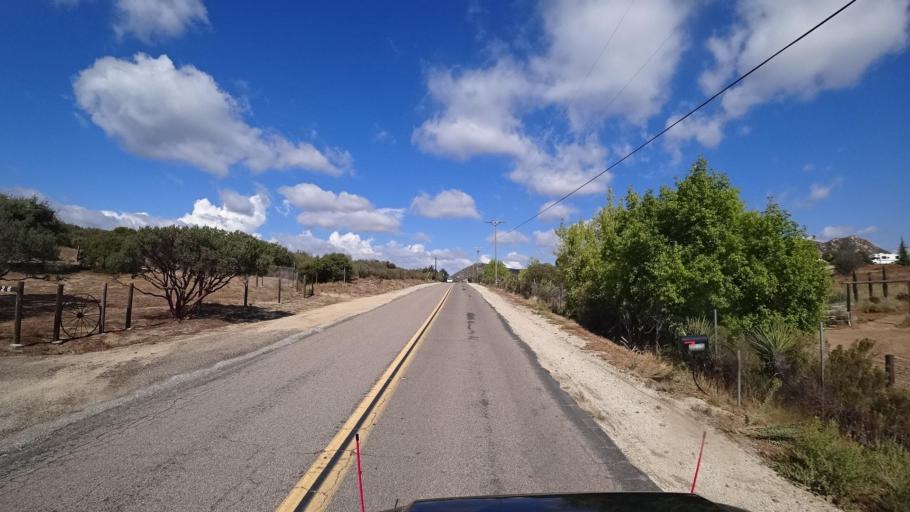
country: US
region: California
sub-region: San Diego County
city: Campo
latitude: 32.6832
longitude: -116.4988
